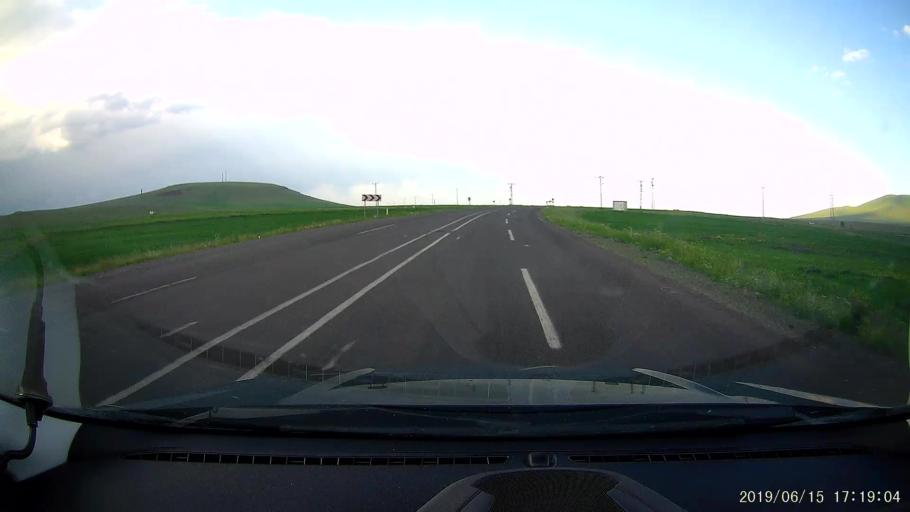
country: TR
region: Kars
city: Kars
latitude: 40.6155
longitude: 43.2708
